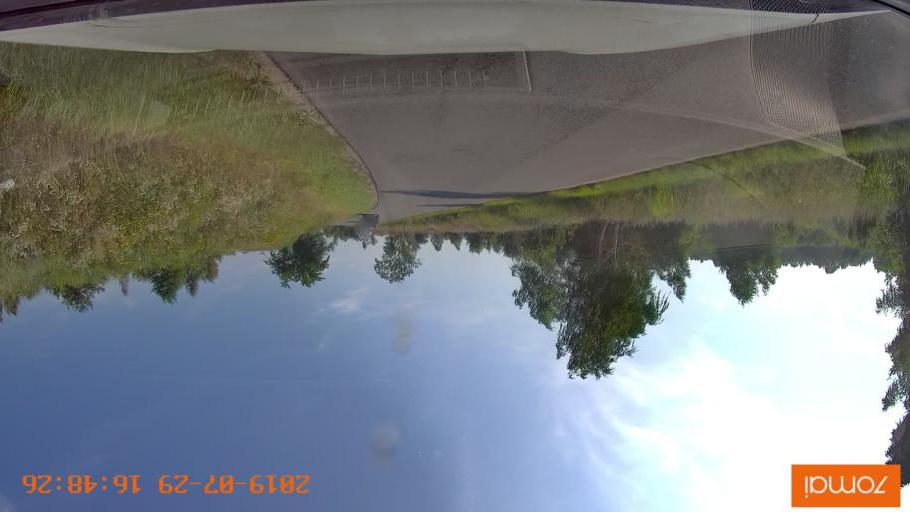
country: RU
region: Kaliningrad
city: Primorsk
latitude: 54.7867
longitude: 20.0772
